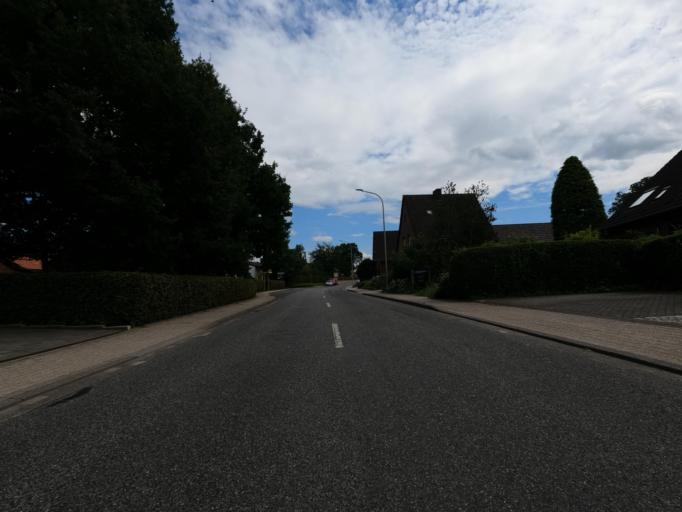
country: DE
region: North Rhine-Westphalia
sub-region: Regierungsbezirk Koln
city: Ubach-Palenberg
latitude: 50.9435
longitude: 6.1543
